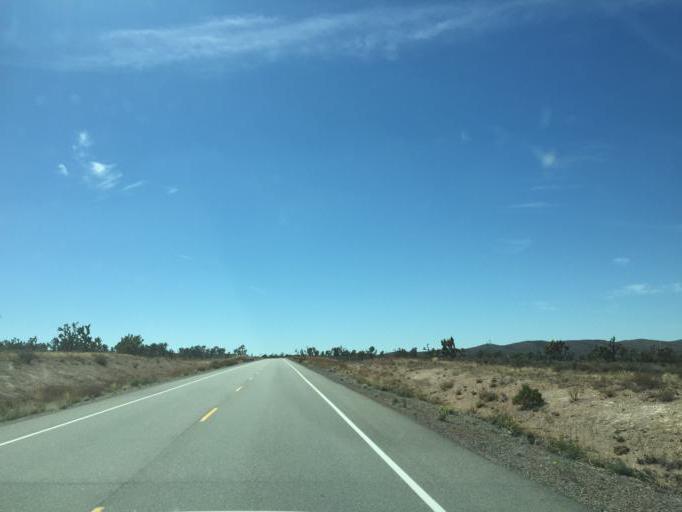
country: US
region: Arizona
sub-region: Mohave County
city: Meadview
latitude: 35.8763
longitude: -114.0573
